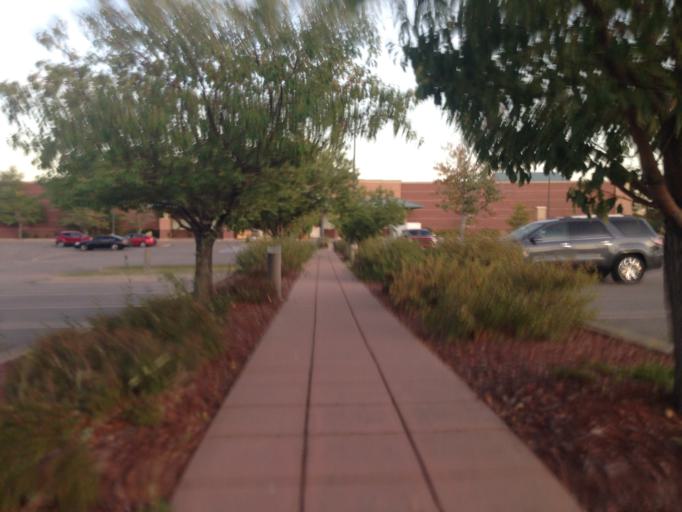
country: US
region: Colorado
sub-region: Boulder County
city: Superior
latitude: 39.9612
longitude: -105.1619
